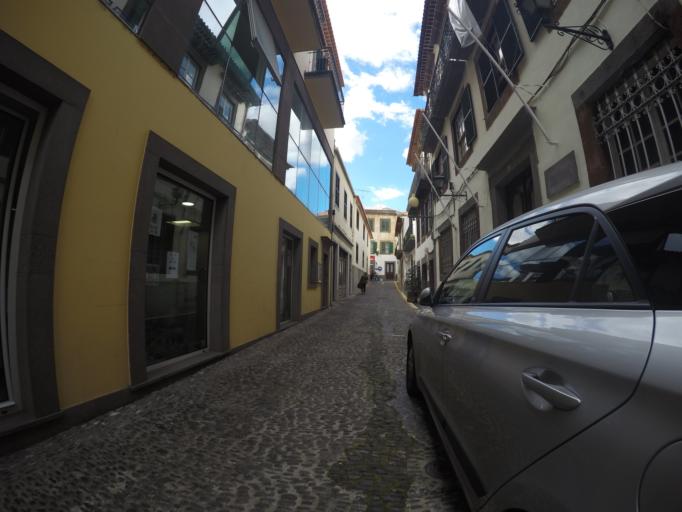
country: PT
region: Madeira
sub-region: Funchal
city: Funchal
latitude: 32.6481
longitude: -16.9127
